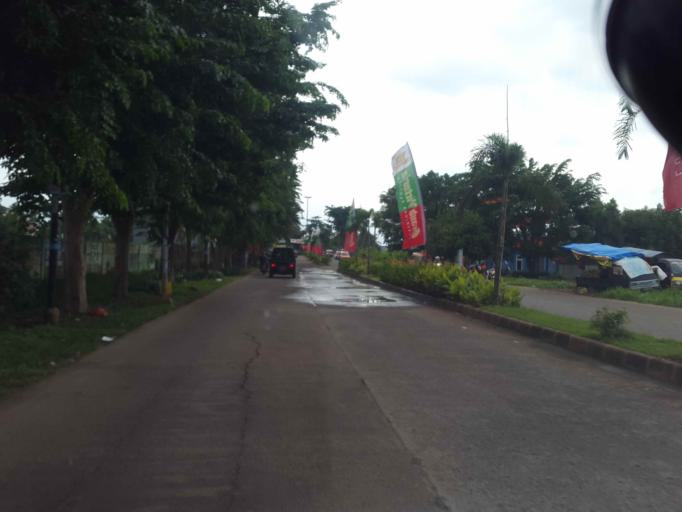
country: ID
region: West Java
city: Cileungsir
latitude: -6.3440
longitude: 106.9437
